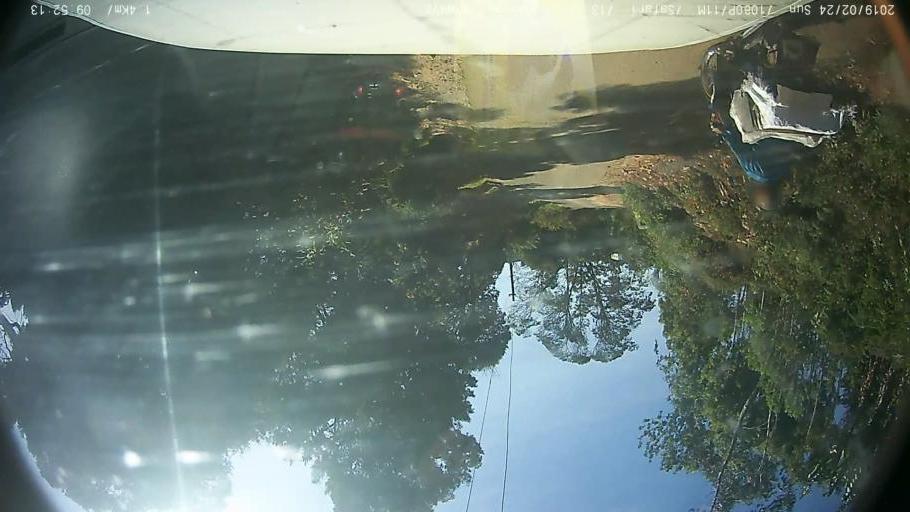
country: IN
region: Tamil Nadu
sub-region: Nilgiri
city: Wellington
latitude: 11.3527
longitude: 76.7738
